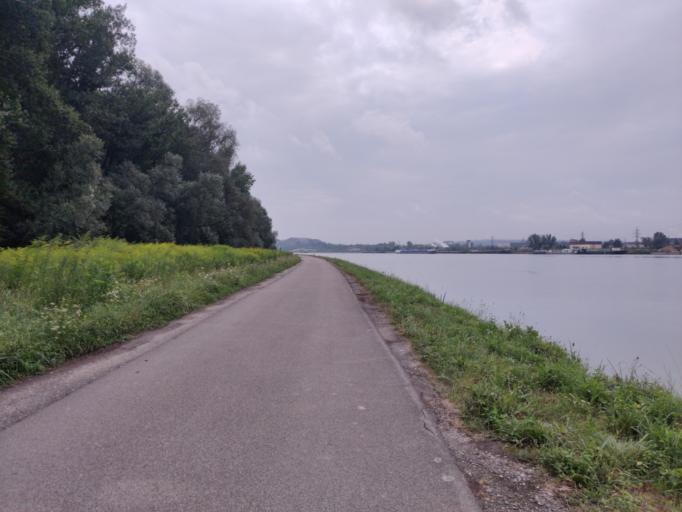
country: AT
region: Upper Austria
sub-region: Politischer Bezirk Urfahr-Umgebung
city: Steyregg
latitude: 48.2849
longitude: 14.3465
